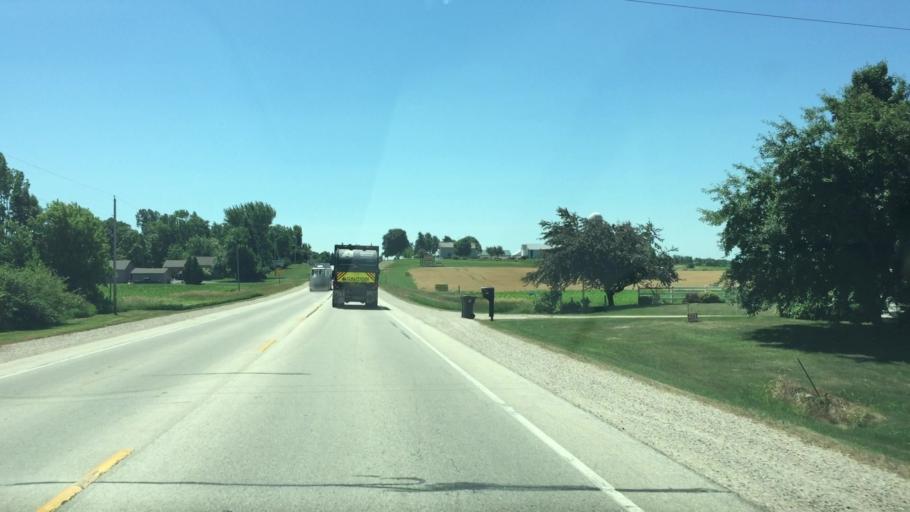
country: US
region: Wisconsin
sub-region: Calumet County
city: Chilton
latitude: 44.0505
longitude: -88.1630
